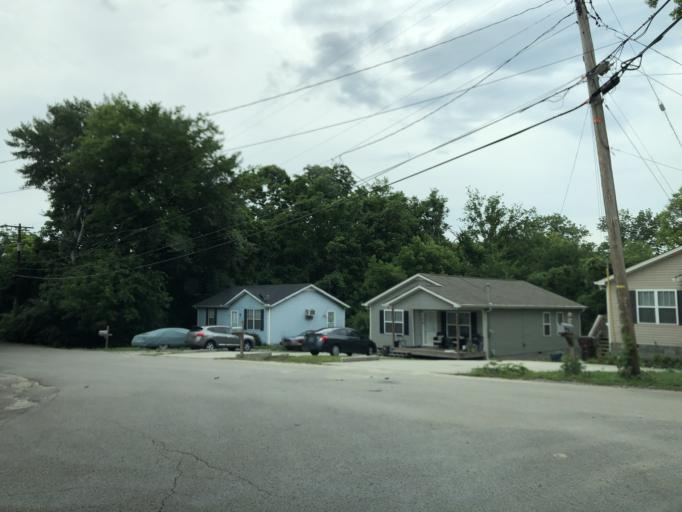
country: US
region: Tennessee
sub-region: Davidson County
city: Goodlettsville
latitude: 36.2796
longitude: -86.7065
